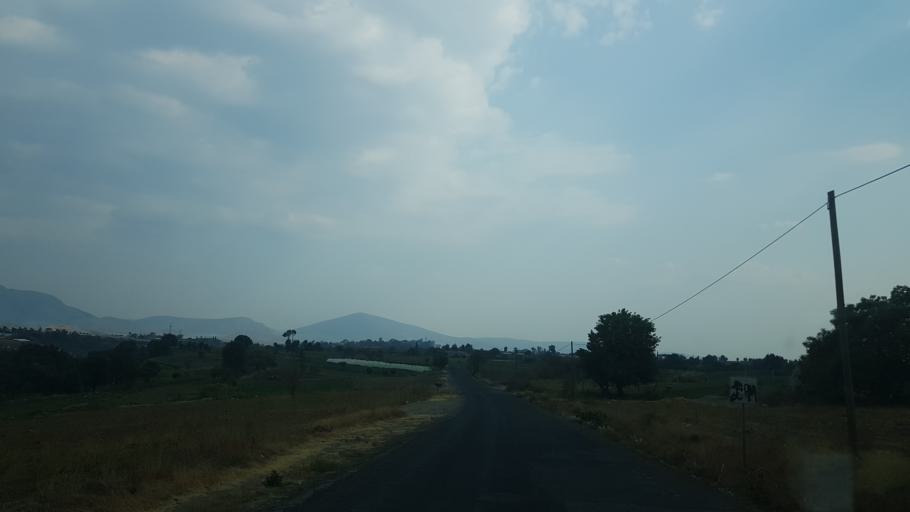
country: MX
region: Puebla
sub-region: Santa Isabel Cholula
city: San Martin Tlamapa
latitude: 18.9662
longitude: -98.3958
